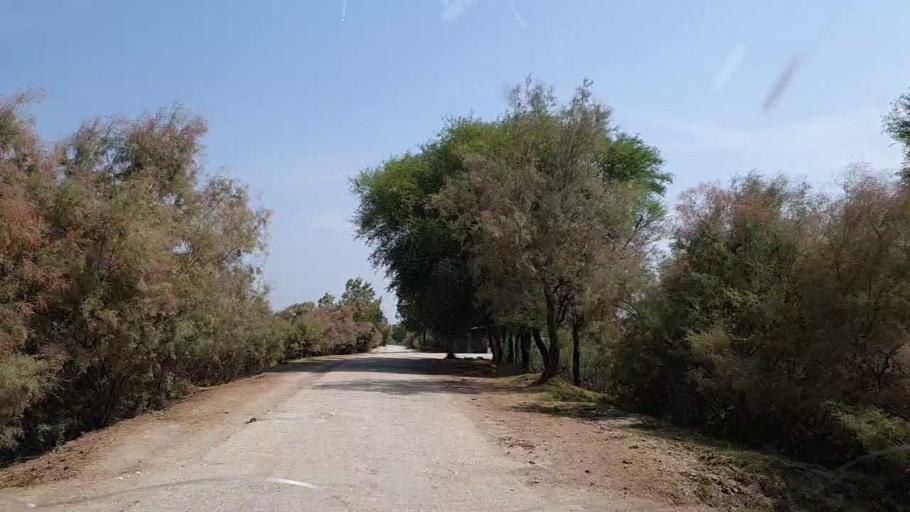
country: PK
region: Sindh
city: Khanpur
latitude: 27.8203
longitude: 69.3044
